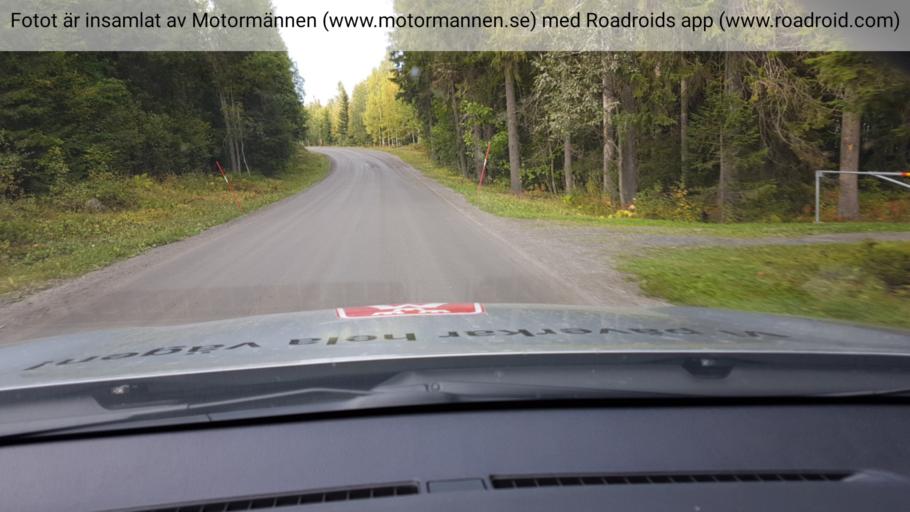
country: SE
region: Jaemtland
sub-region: Stroemsunds Kommun
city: Stroemsund
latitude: 64.0010
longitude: 15.8165
